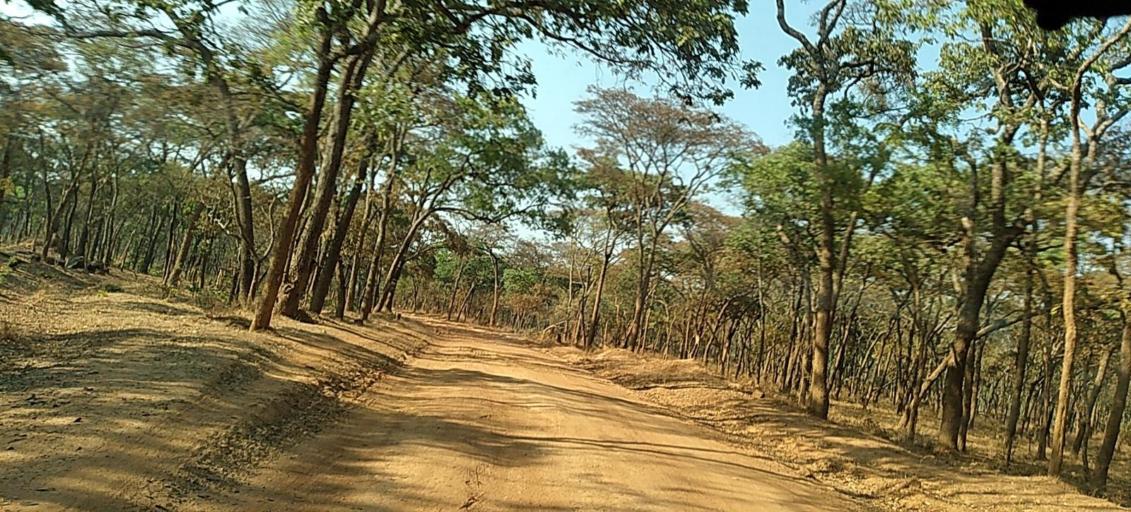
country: ZM
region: North-Western
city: Kasempa
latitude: -13.6048
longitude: 25.9772
